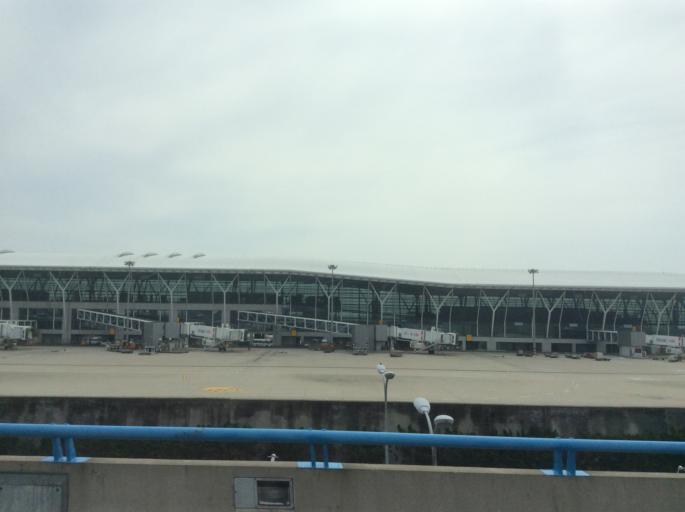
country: CN
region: Shanghai Shi
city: Laogang
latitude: 31.1480
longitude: 121.8057
